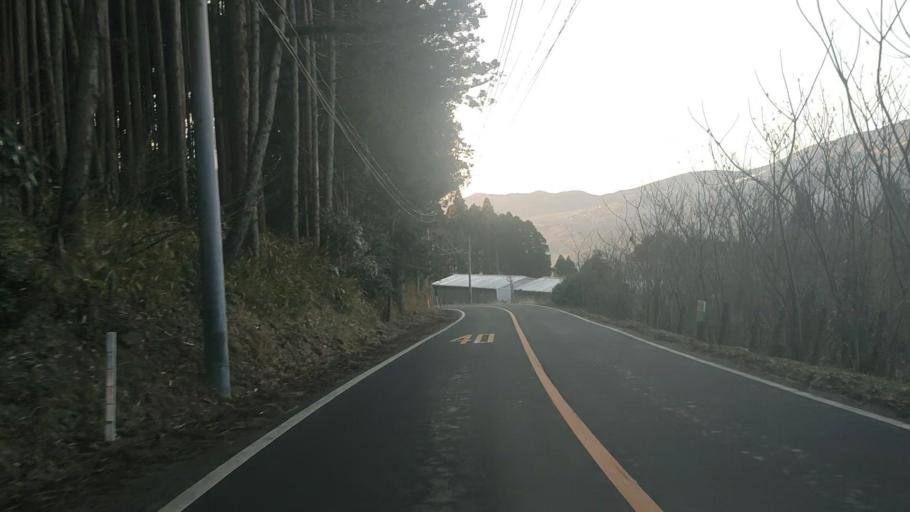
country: JP
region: Oita
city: Beppu
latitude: 33.2554
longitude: 131.3720
